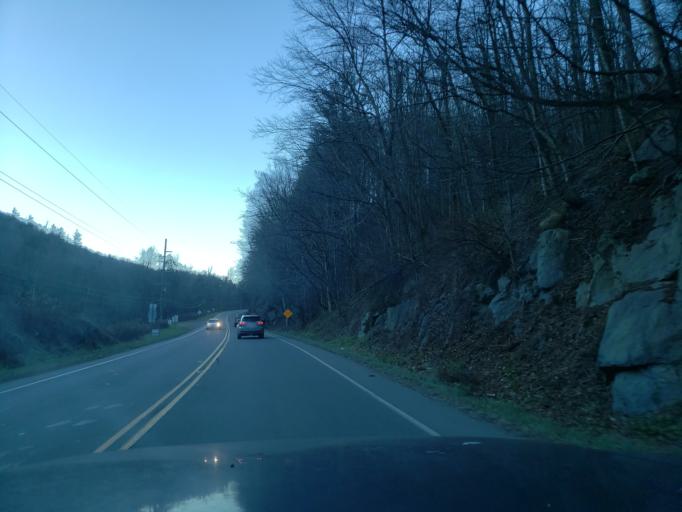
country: US
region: North Carolina
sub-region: Watauga County
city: Foscoe
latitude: 36.1933
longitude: -81.7456
